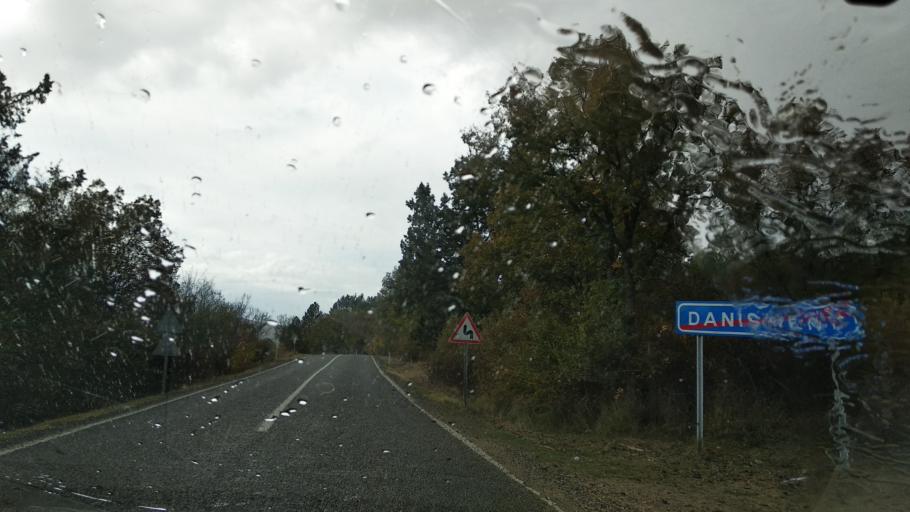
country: TR
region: Ankara
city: Nallihan
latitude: 40.3281
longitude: 31.4092
